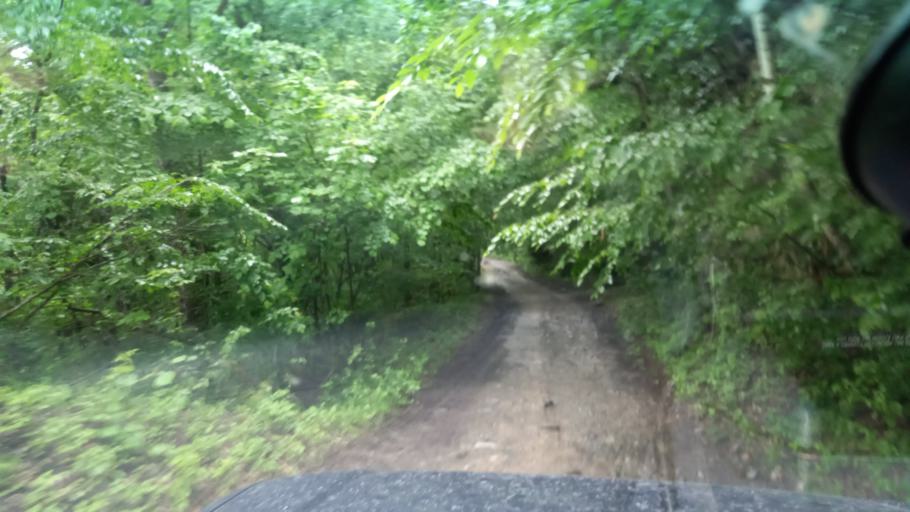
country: RU
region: Krasnodarskiy
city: Psebay
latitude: 44.0079
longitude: 40.7063
